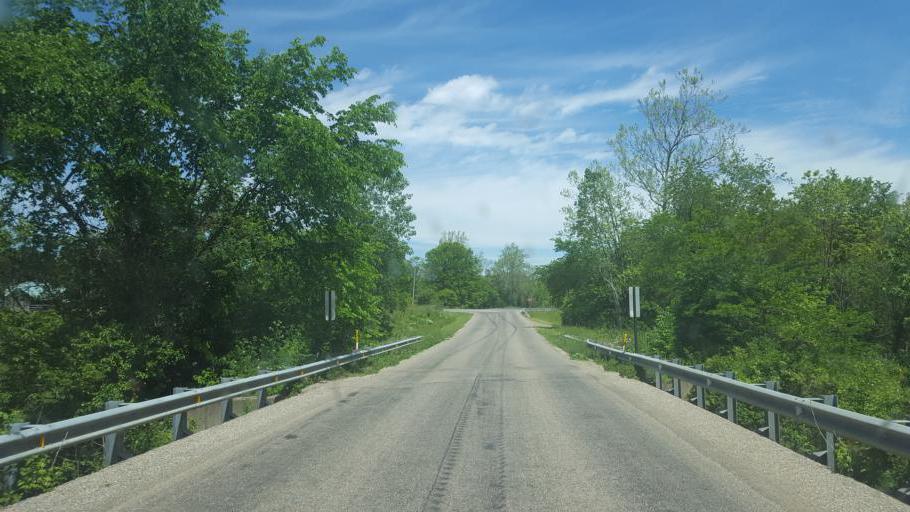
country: US
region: Ohio
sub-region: Knox County
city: Danville
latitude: 40.4053
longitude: -82.3216
